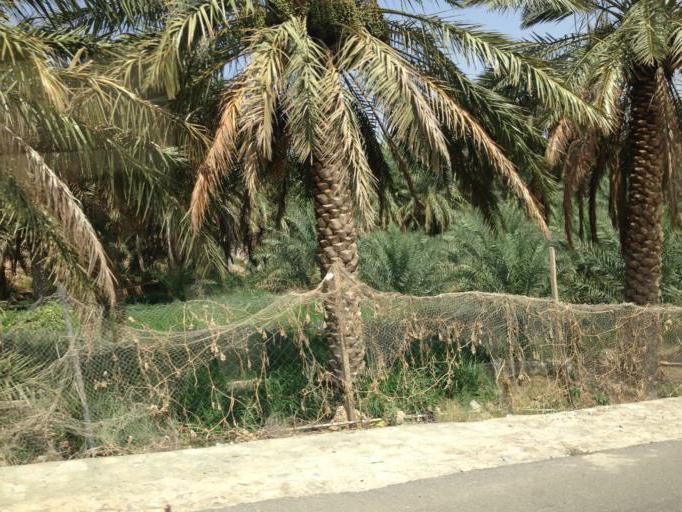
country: OM
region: Ash Sharqiyah
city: Ibra'
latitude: 23.0854
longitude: 58.8644
